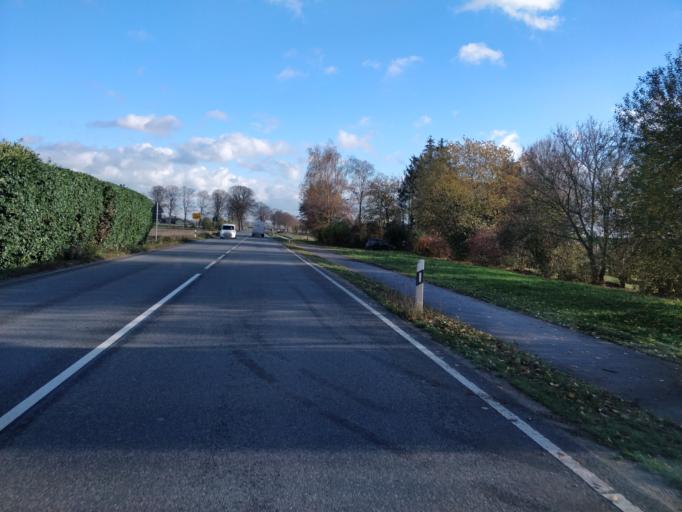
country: NL
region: Gelderland
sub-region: Oude IJsselstreek
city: Gendringen
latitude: 51.8199
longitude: 6.3426
